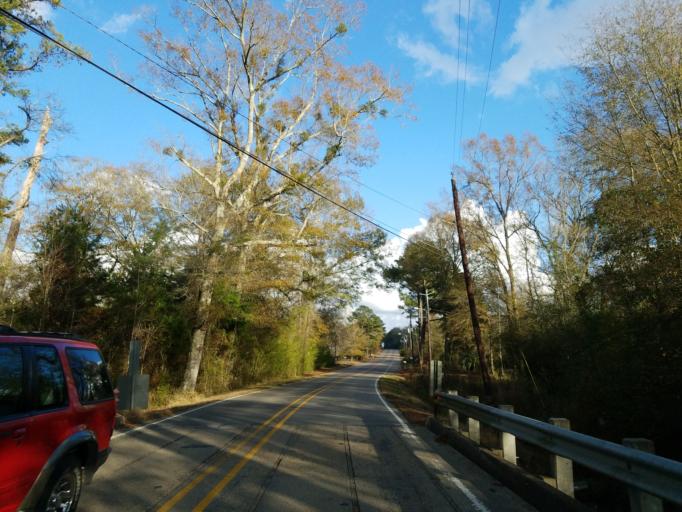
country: US
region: Mississippi
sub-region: Jones County
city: Sharon
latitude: 31.7881
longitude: -89.0468
